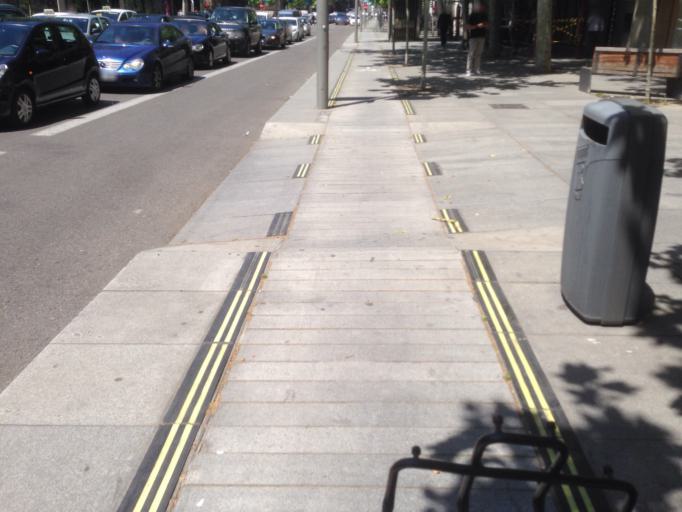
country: ES
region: Madrid
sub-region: Provincia de Madrid
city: Salamanca
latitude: 40.4232
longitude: -3.6882
